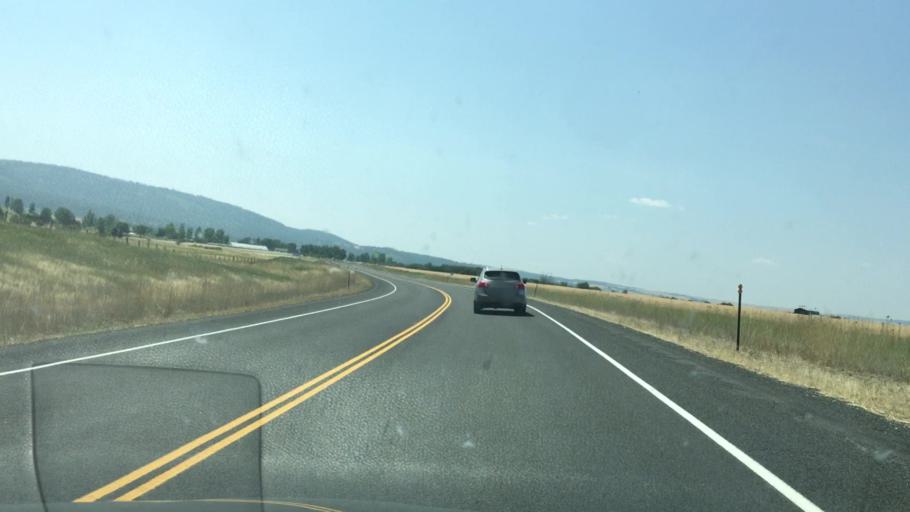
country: US
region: Idaho
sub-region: Idaho County
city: Grangeville
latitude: 45.9208
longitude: -116.1561
